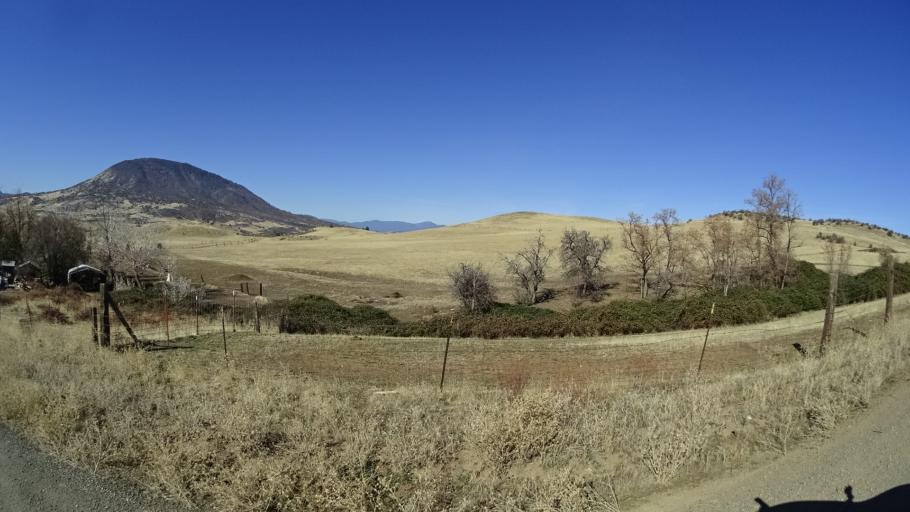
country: US
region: California
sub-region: Siskiyou County
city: Montague
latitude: 41.8450
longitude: -122.4423
